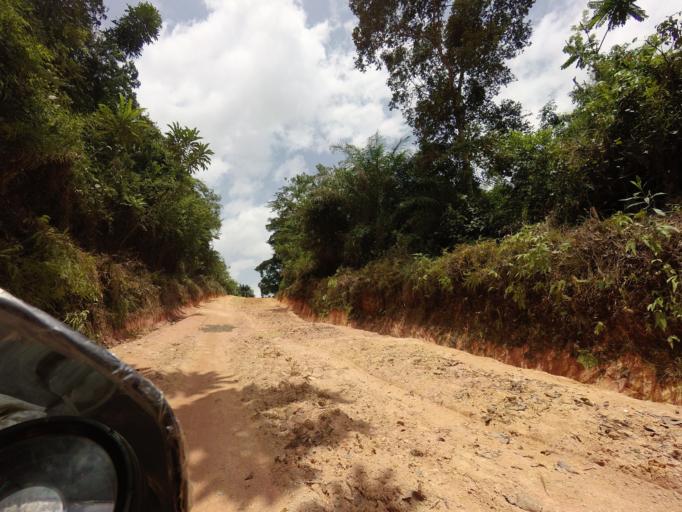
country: SL
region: Eastern Province
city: Kailahun
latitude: 8.3599
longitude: -10.7151
